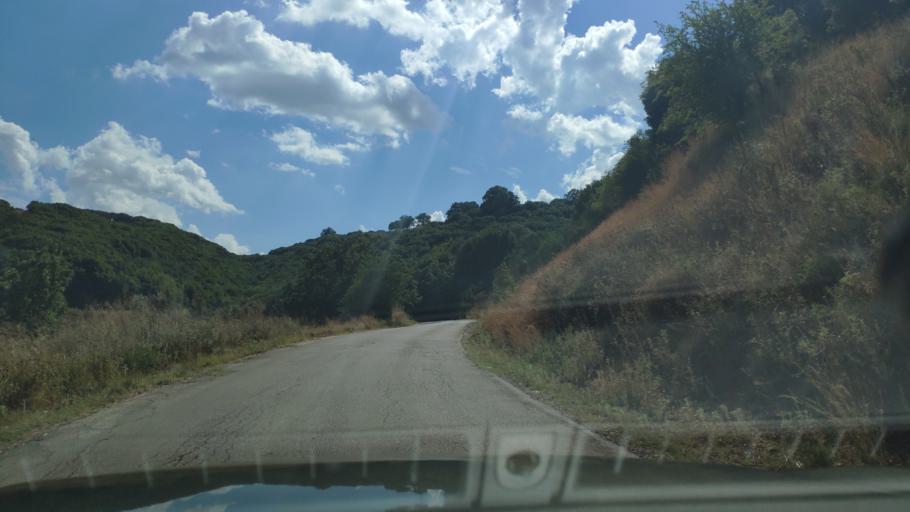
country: GR
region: West Greece
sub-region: Nomos Aitolias kai Akarnanias
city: Katouna
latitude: 38.8048
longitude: 21.1117
